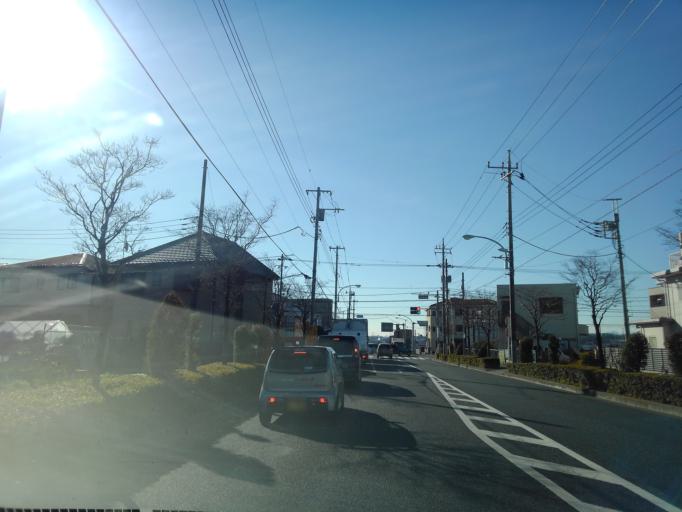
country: JP
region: Tokyo
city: Hino
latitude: 35.7022
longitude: 139.3775
